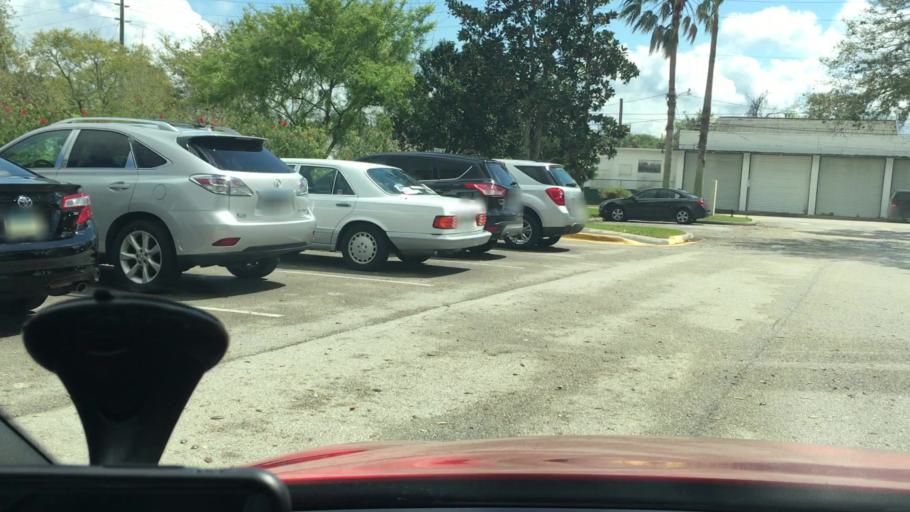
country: US
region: Florida
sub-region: Volusia County
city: New Smyrna Beach
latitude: 29.0196
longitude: -80.9216
